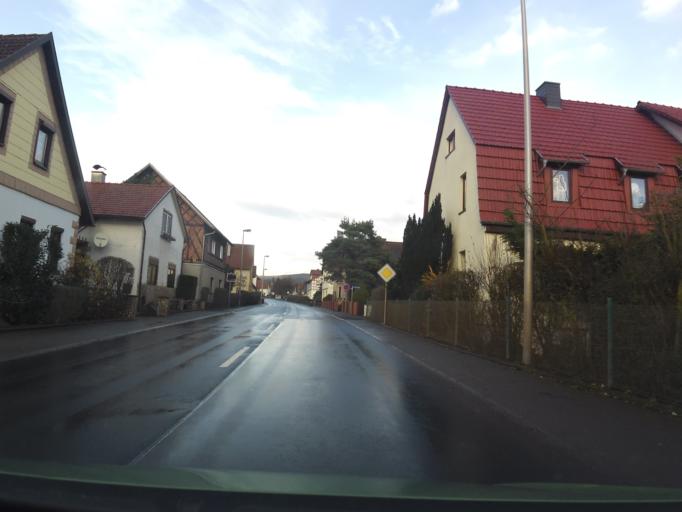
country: DE
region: Thuringia
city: Barchfeld
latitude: 50.8335
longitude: 10.2894
